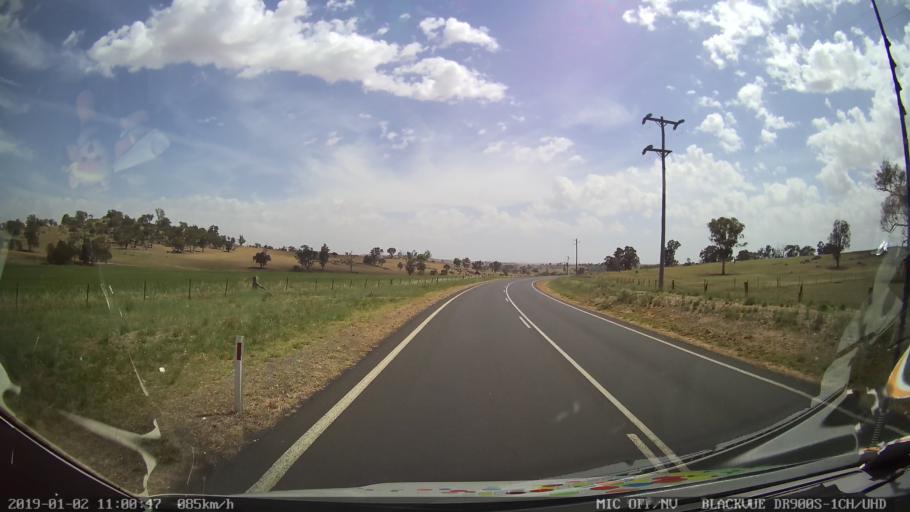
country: AU
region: New South Wales
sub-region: Cootamundra
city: Cootamundra
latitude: -34.6044
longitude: 148.3136
